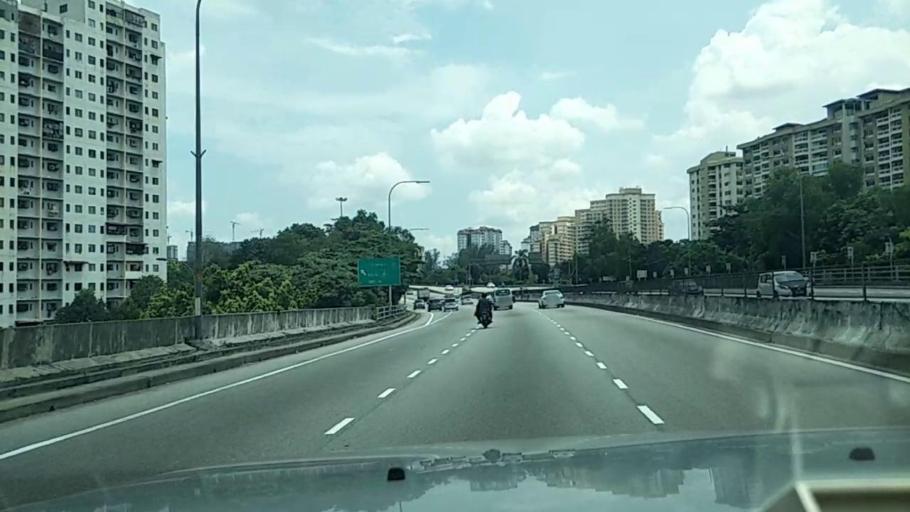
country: MY
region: Selangor
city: Kampong Baharu Balakong
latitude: 3.0662
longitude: 101.7069
